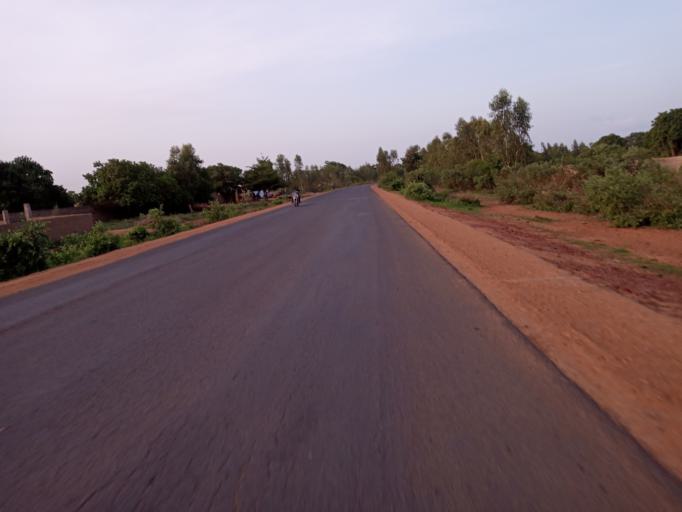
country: ML
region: Bamako
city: Bamako
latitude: 12.2953
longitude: -8.1645
